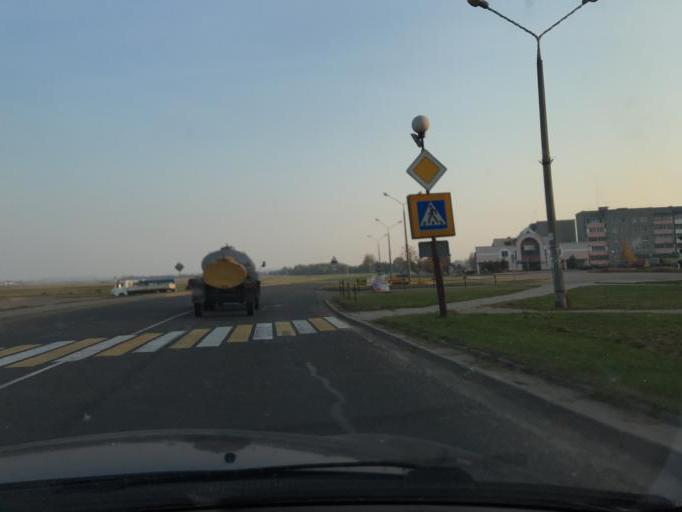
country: BY
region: Grodnenskaya
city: Karelichy
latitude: 53.5704
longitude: 26.1453
